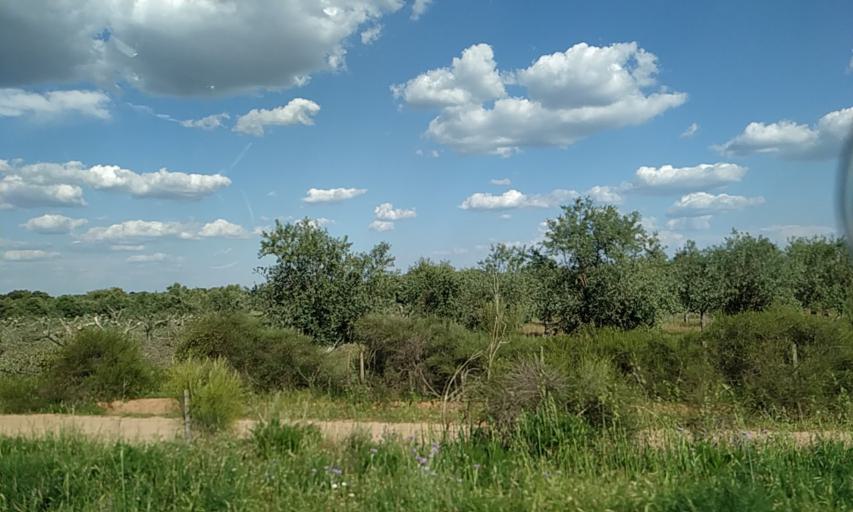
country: PT
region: Evora
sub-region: Estremoz
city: Estremoz
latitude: 38.8871
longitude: -7.5566
